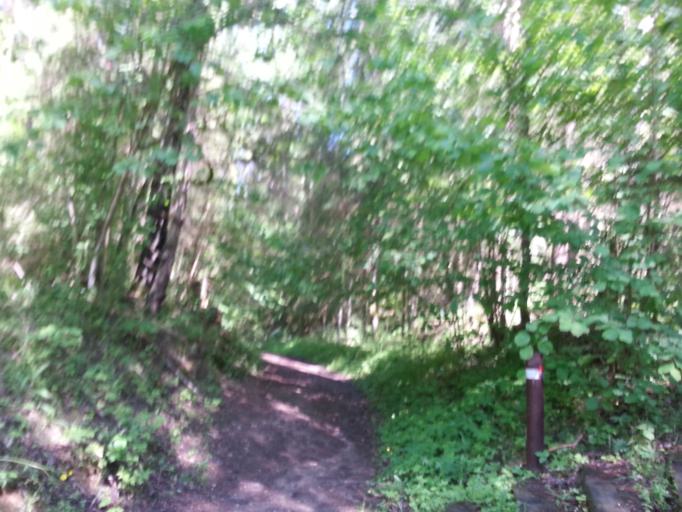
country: BY
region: Vitebsk
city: Lyntupy
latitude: 54.9603
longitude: 26.3614
